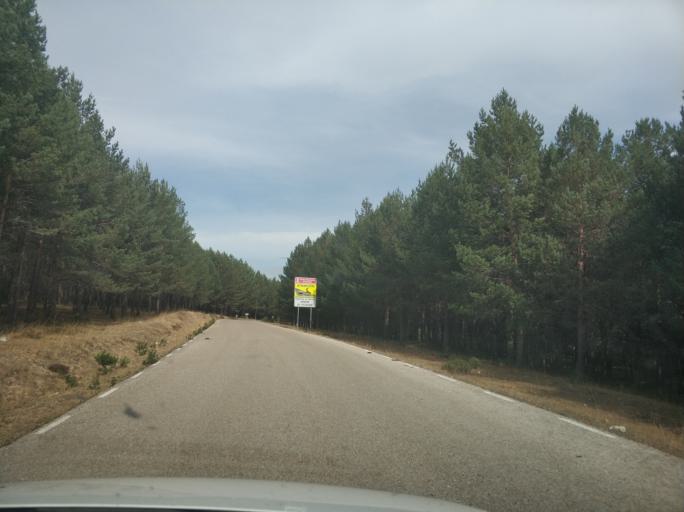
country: ES
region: Castille and Leon
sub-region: Provincia de Soria
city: Duruelo de la Sierra
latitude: 41.8779
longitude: -2.9374
